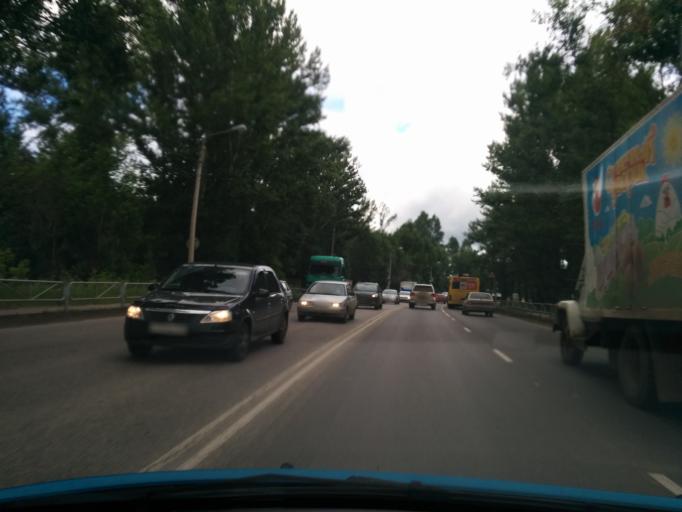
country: RU
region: Perm
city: Kondratovo
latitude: 58.0418
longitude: 56.0470
